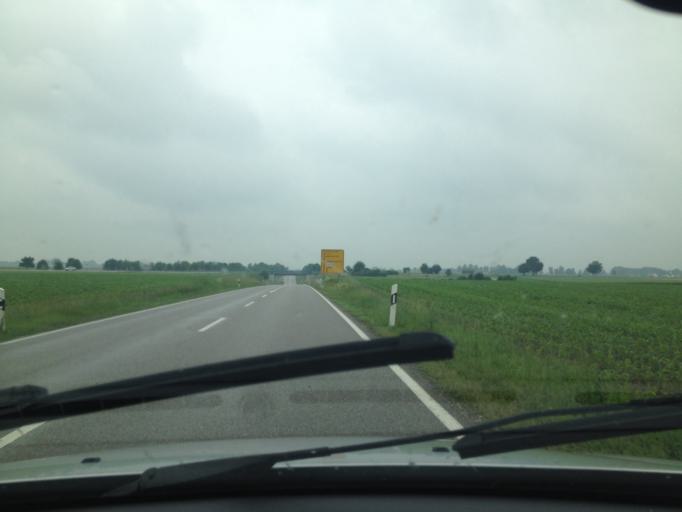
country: DE
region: Bavaria
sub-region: Swabia
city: Langerringen
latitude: 48.1699
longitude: 10.7822
